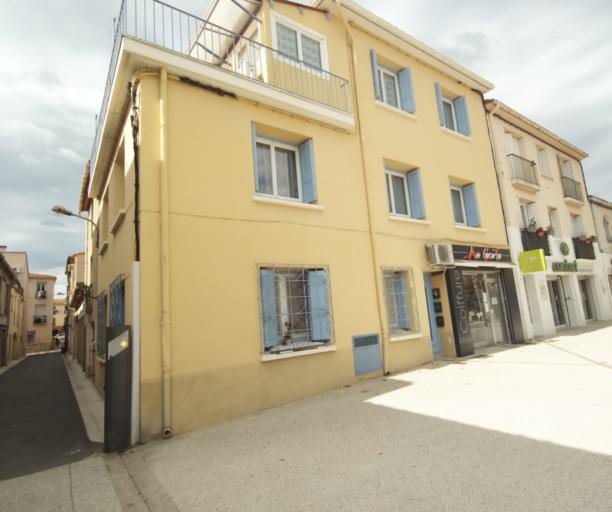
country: FR
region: Languedoc-Roussillon
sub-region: Departement des Pyrenees-Orientales
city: Argelers
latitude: 42.5458
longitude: 3.0242
